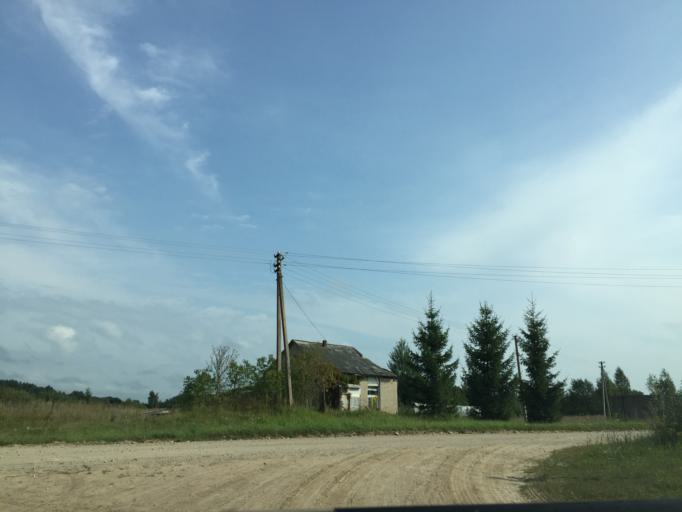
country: LV
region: Dagda
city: Dagda
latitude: 56.3015
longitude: 27.6527
